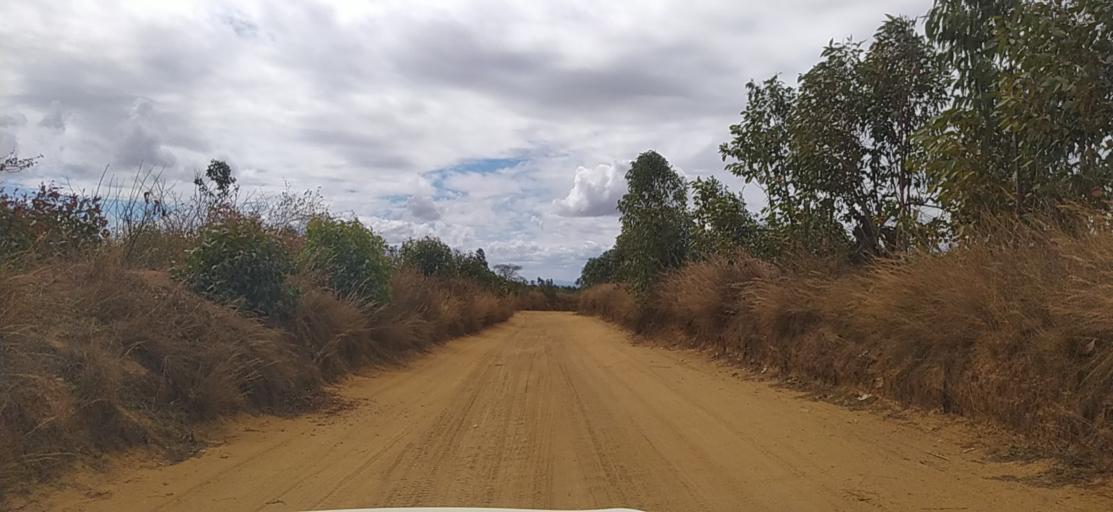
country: MG
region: Alaotra Mangoro
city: Ambatondrazaka
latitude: -17.9471
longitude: 48.2484
